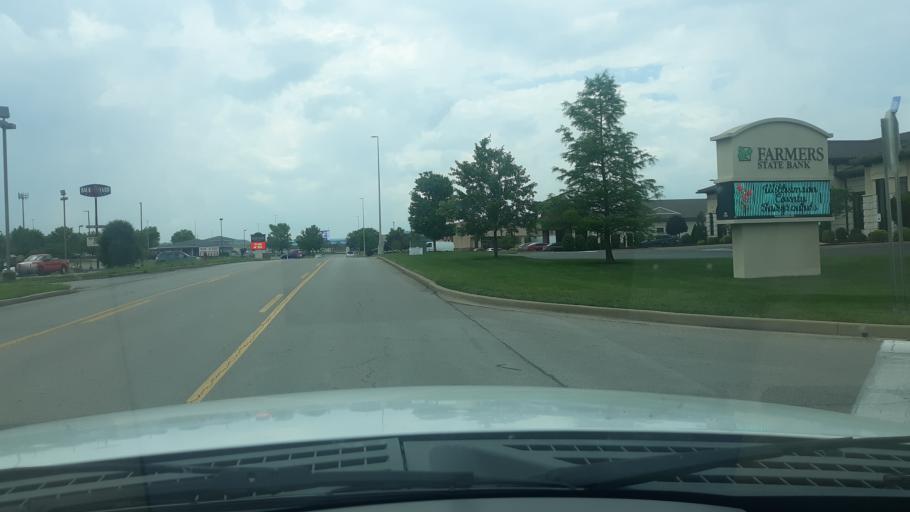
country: US
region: Illinois
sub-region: Williamson County
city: Marion
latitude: 37.7453
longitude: -88.9716
